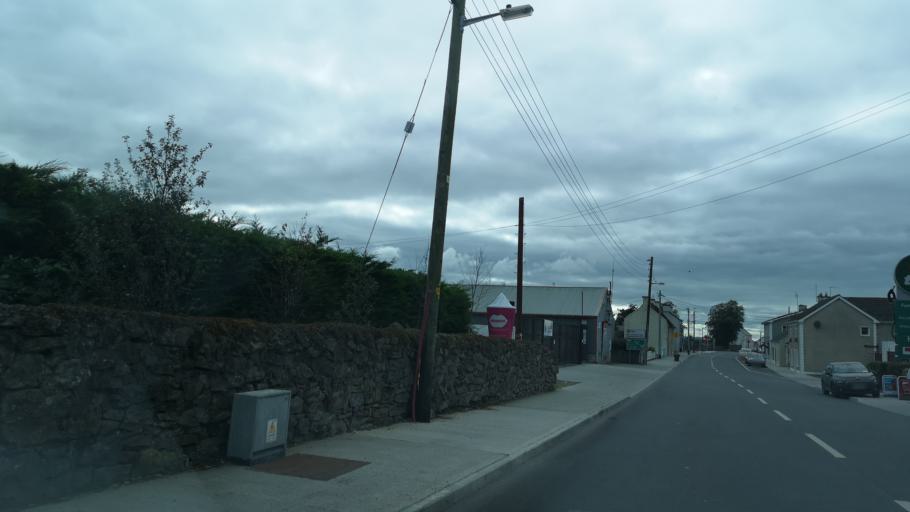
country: IE
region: Leinster
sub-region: Uibh Fhaili
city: Ferbane
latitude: 53.2247
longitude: -7.8801
